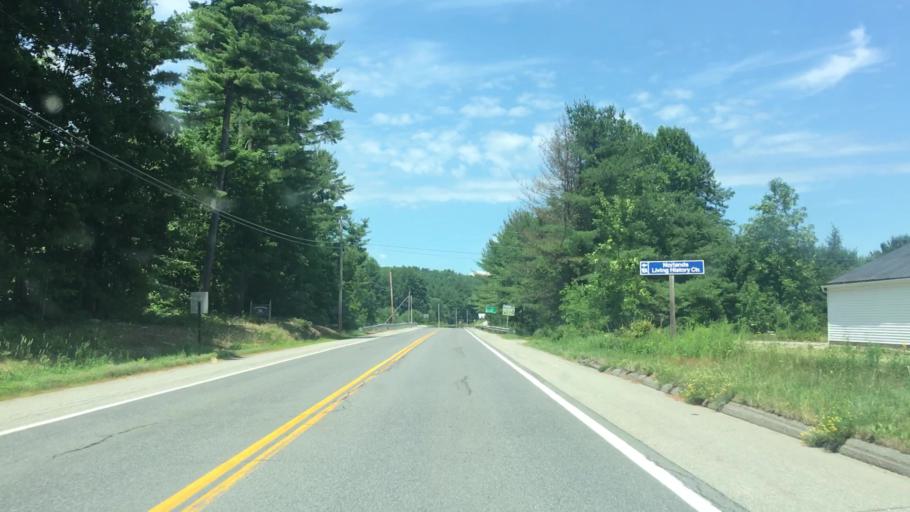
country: US
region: Maine
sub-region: Kennebec County
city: Wayne
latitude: 44.3565
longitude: -70.0801
